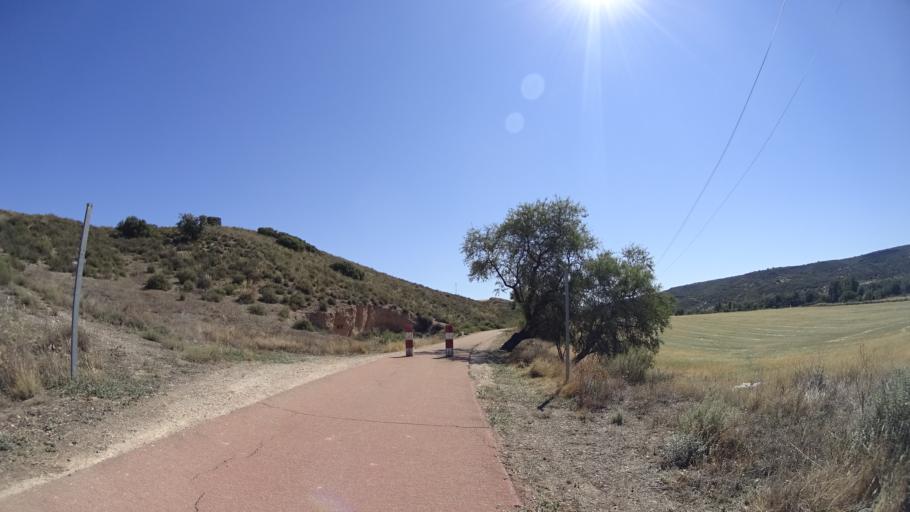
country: ES
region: Madrid
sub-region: Provincia de Madrid
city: Morata de Tajuna
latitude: 40.2324
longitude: -3.3959
